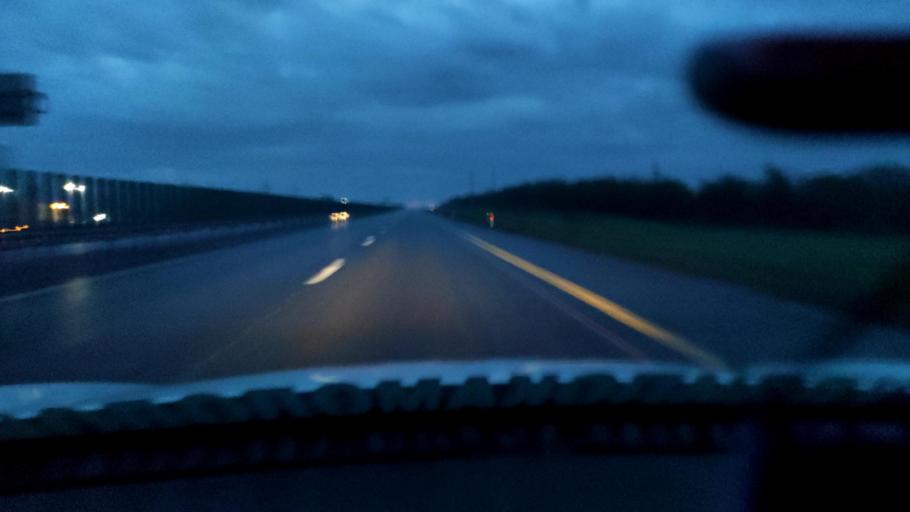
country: RU
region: Rostov
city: Glubokiy
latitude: 48.5437
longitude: 40.3473
